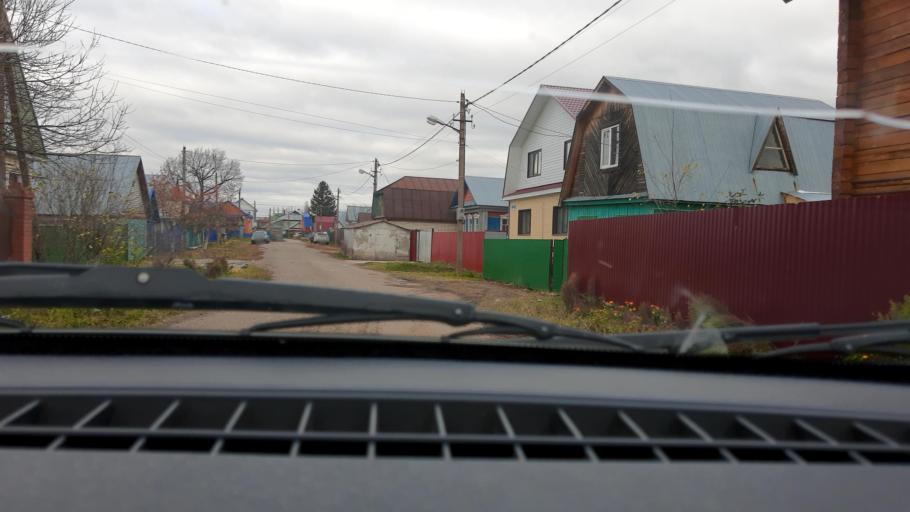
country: RU
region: Bashkortostan
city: Ufa
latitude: 54.7407
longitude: 55.9073
